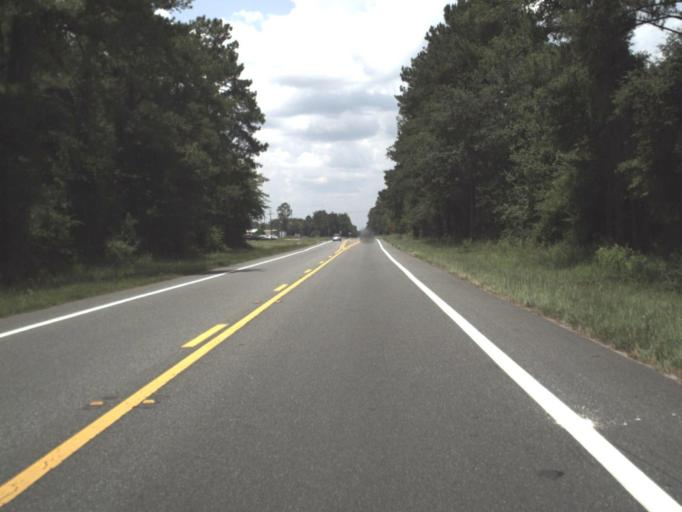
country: US
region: Florida
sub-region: Columbia County
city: Five Points
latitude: 30.2238
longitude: -82.6596
